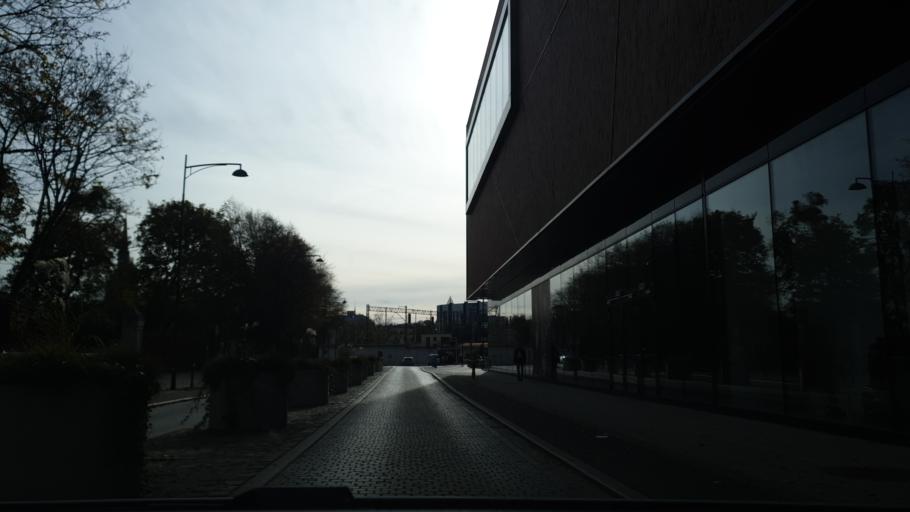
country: PL
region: Pomeranian Voivodeship
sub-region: Gdansk
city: Gdansk
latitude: 54.3827
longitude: 18.6066
